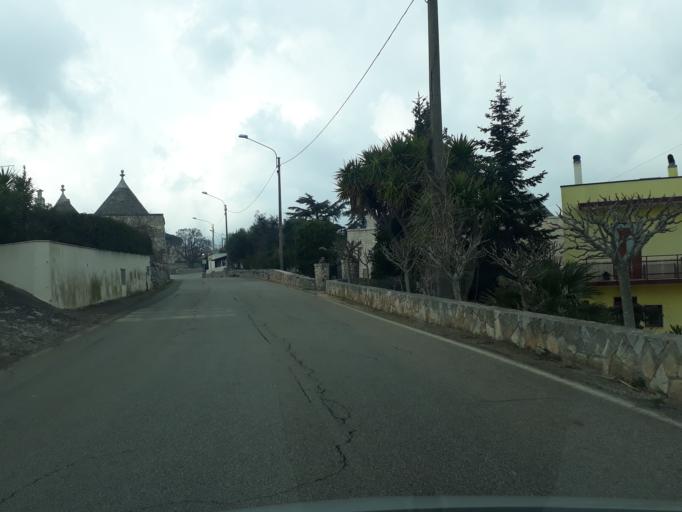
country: IT
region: Apulia
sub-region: Provincia di Brindisi
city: Lamie di Olimpie-Selva
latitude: 40.7904
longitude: 17.3217
